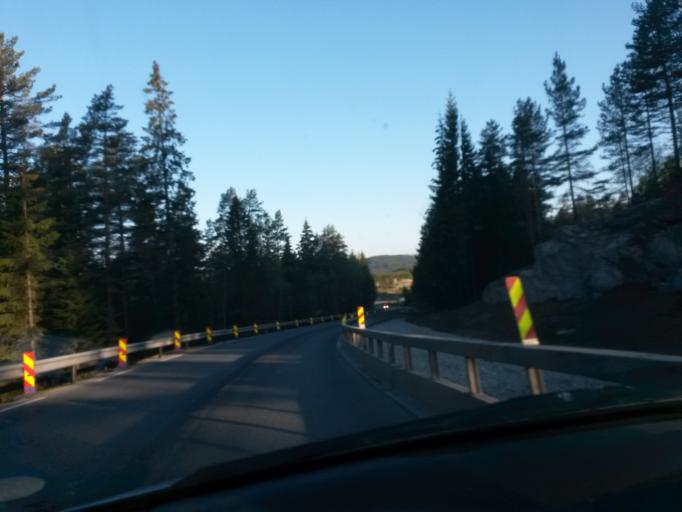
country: NO
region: Telemark
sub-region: Notodden
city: Notodden
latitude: 59.5827
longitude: 9.3146
